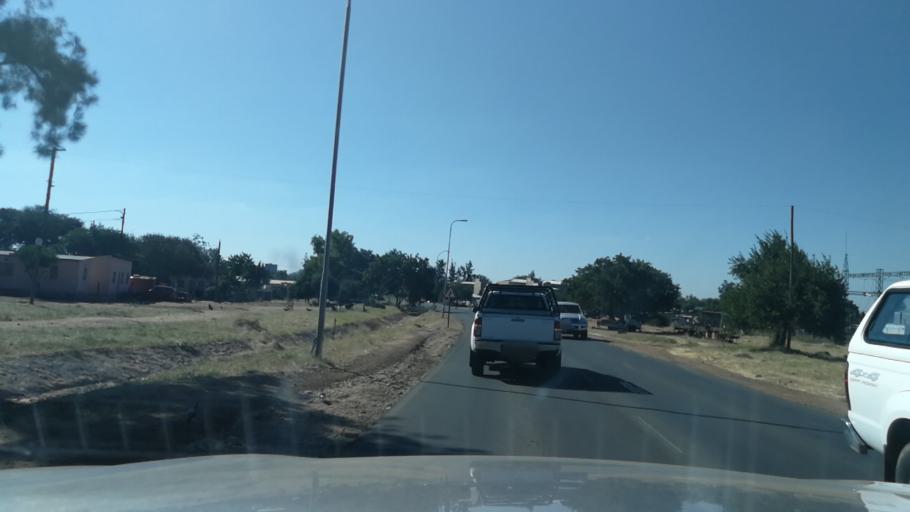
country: BW
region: South East
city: Gaborone
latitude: -24.6863
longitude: 25.9048
